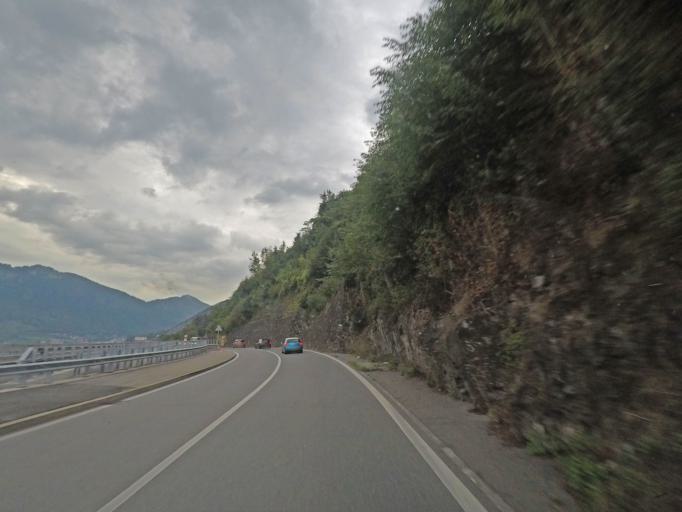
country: CH
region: Schwyz
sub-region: Bezirk Schwyz
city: Ingenbohl
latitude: 46.9734
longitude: 8.6111
